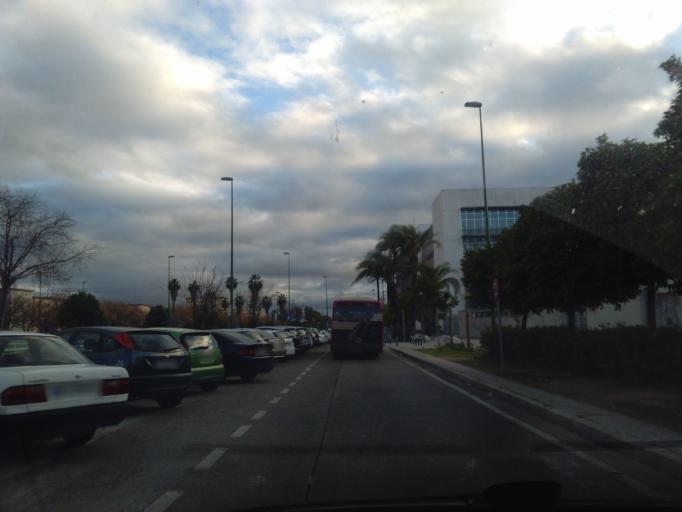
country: ES
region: Andalusia
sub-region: Provincia de Sevilla
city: Sevilla
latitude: 37.3865
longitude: -5.9596
